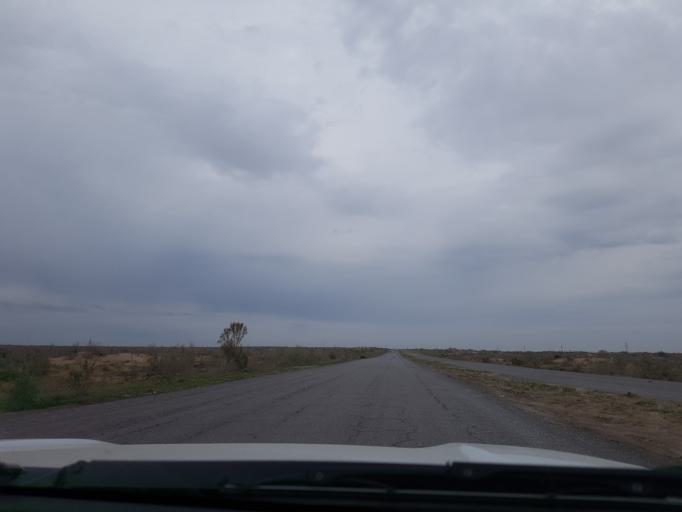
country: TM
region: Lebap
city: Turkmenabat
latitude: 38.9528
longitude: 63.4961
